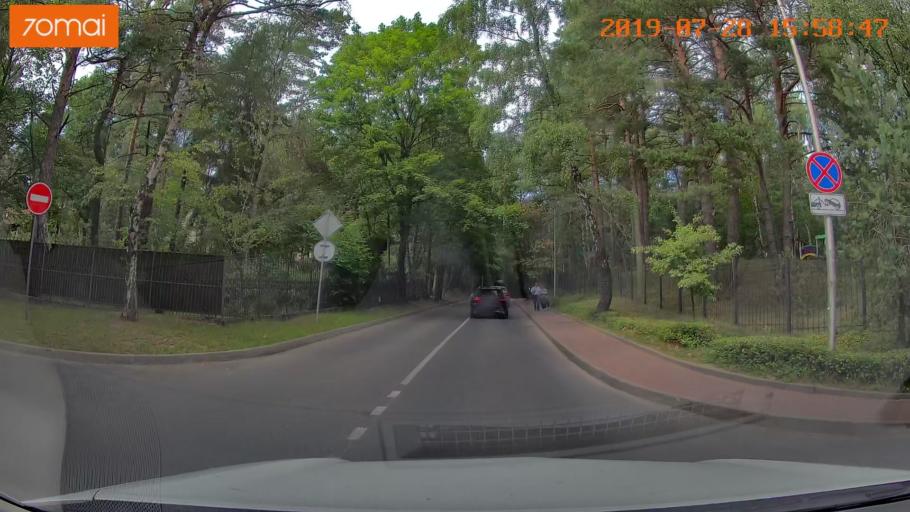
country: RU
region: Kaliningrad
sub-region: Gorod Svetlogorsk
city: Svetlogorsk
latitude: 54.9406
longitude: 20.1618
